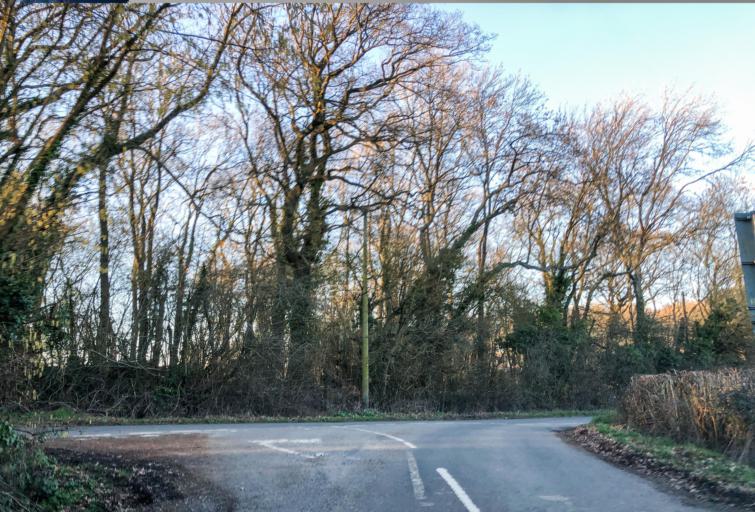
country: GB
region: England
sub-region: Warwickshire
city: Wroxall
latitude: 52.2820
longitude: -1.6667
